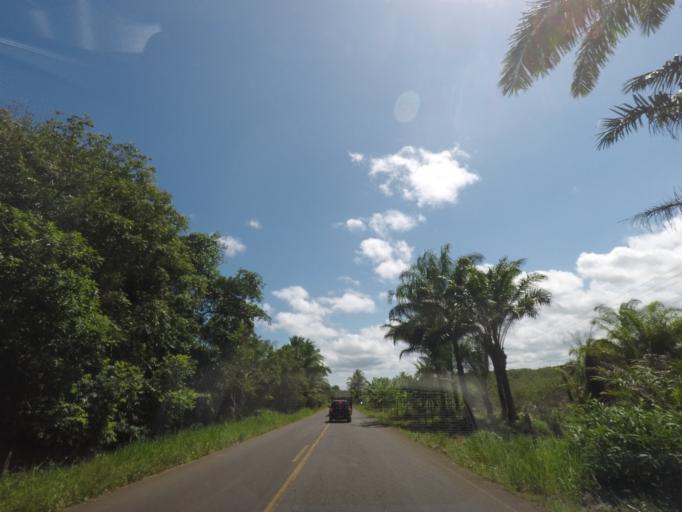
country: BR
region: Bahia
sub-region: Taperoa
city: Taperoa
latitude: -13.4767
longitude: -39.0897
